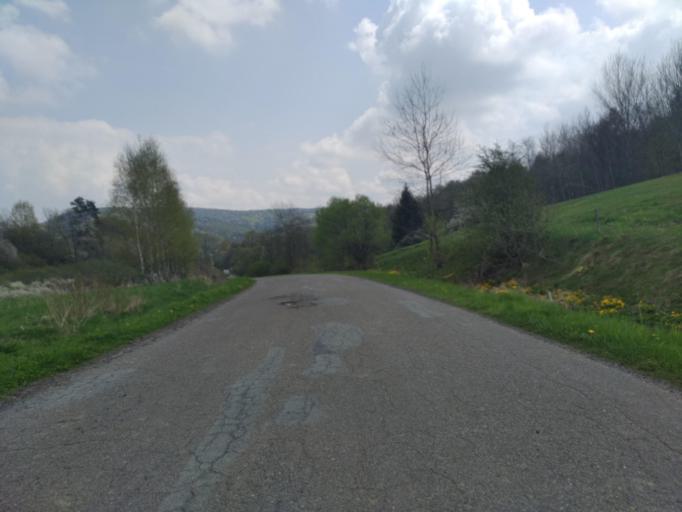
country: PL
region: Subcarpathian Voivodeship
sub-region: Powiat krosnienski
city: Iwonicz-Zdroj
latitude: 49.5251
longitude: 21.8135
